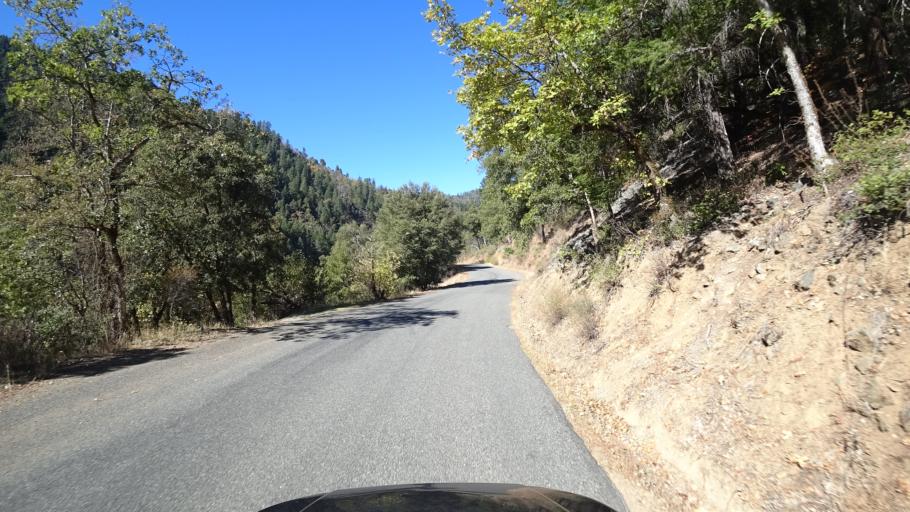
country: US
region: California
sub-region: Humboldt County
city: Willow Creek
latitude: 41.2850
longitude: -123.3599
